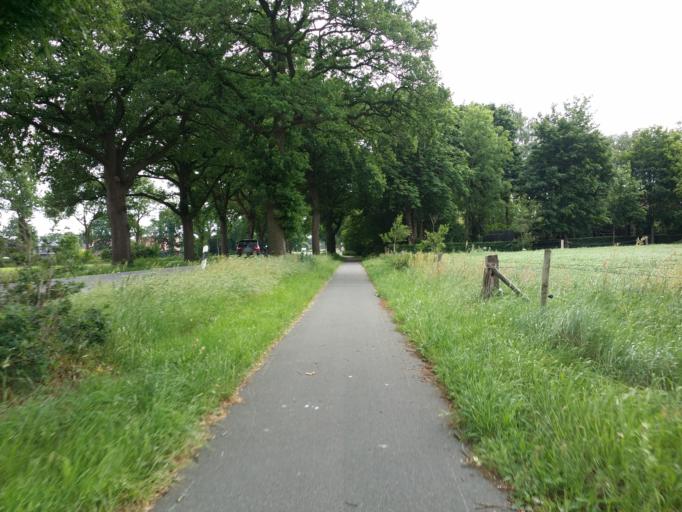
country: DE
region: Lower Saxony
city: Wiefelstede
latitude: 53.2655
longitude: 8.1115
